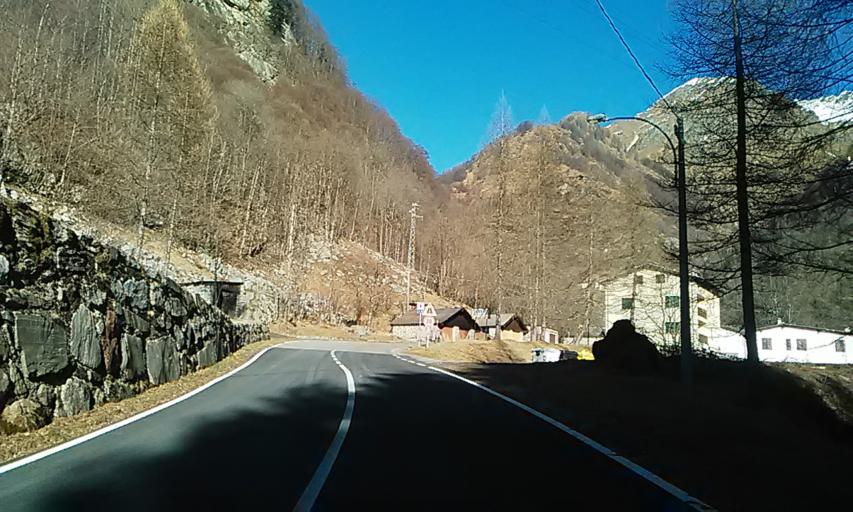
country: IT
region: Piedmont
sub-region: Provincia di Vercelli
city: Rimasco
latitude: 45.8859
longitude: 8.0663
